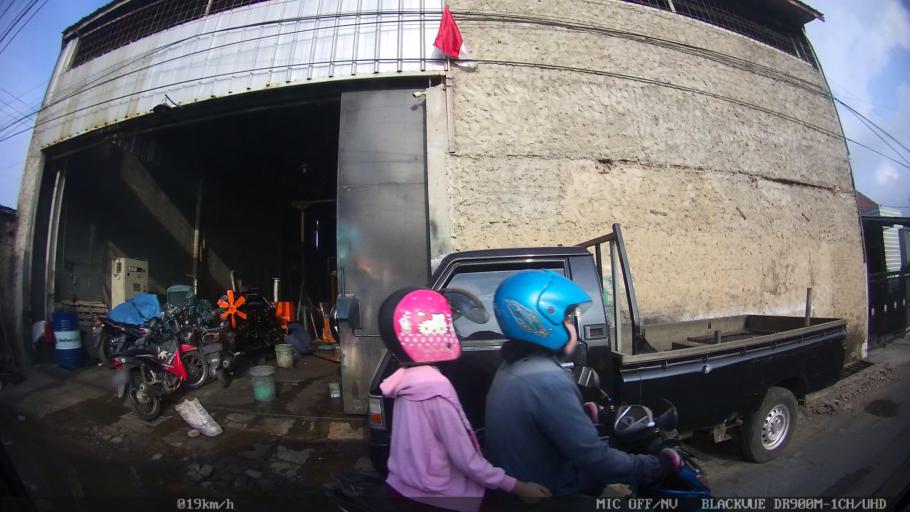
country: ID
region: Lampung
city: Kedaton
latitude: -5.4003
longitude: 105.3085
